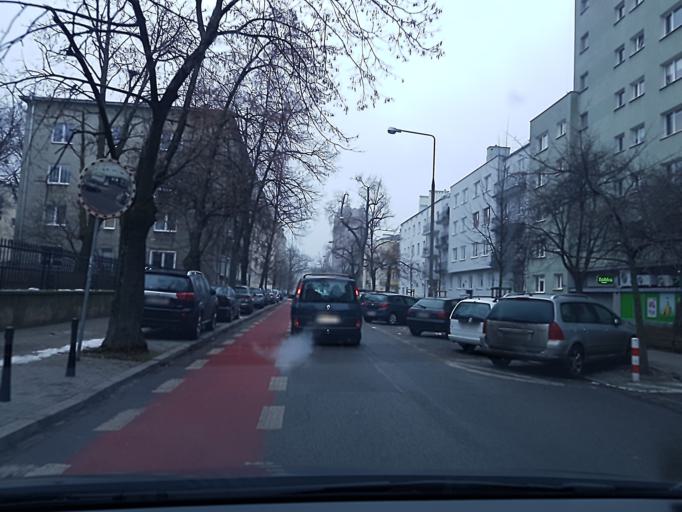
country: PL
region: Masovian Voivodeship
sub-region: Warszawa
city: Srodmiescie
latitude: 52.2070
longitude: 21.0133
